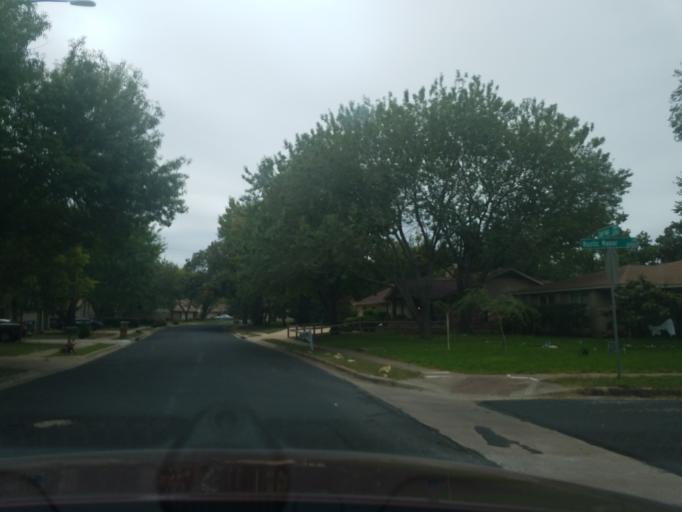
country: US
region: Texas
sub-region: Williamson County
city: Anderson Mill
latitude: 30.4604
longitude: -97.8055
